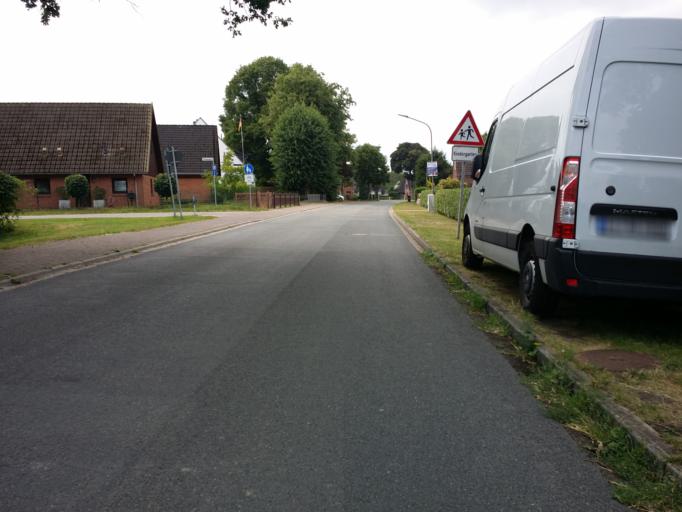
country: DE
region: Schleswig-Holstein
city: Heiligenstedtenerkamp
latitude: 53.9000
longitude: 9.4689
